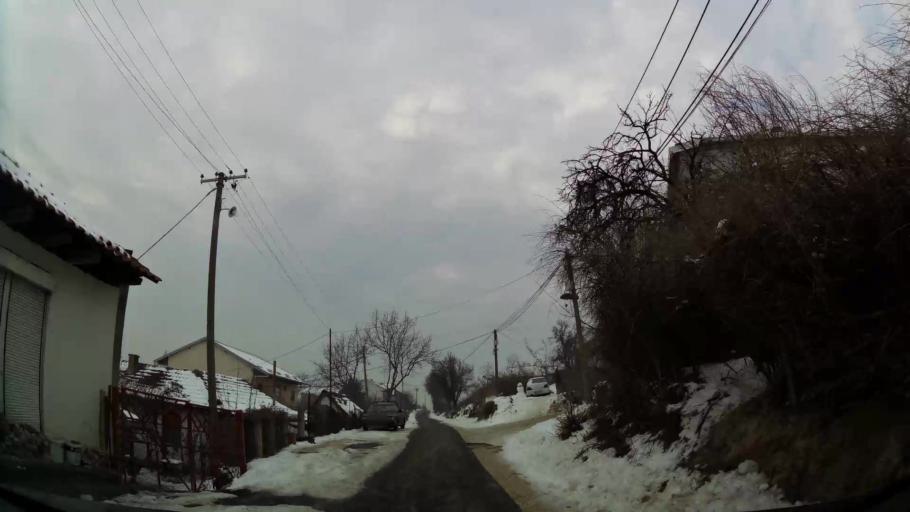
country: MK
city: Kondovo
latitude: 42.0409
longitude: 21.3436
